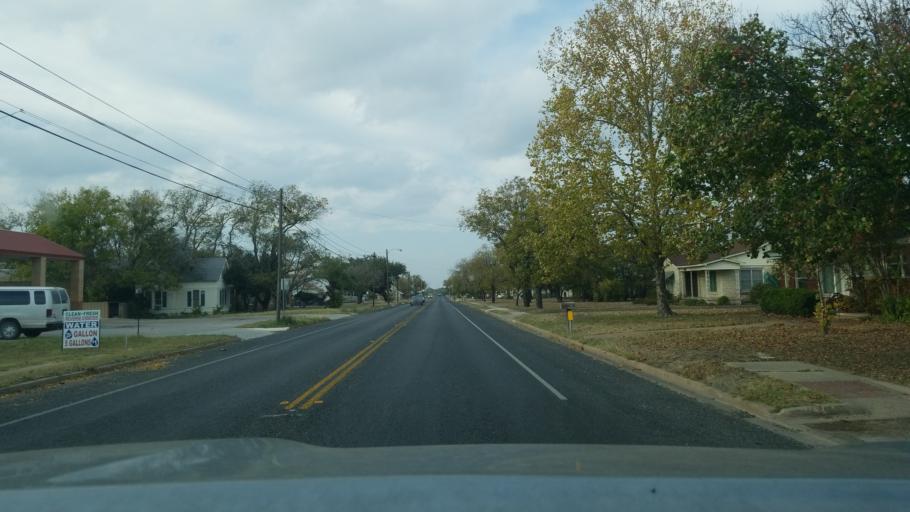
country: US
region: Texas
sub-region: Mills County
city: Goldthwaite
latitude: 31.4562
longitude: -98.5717
